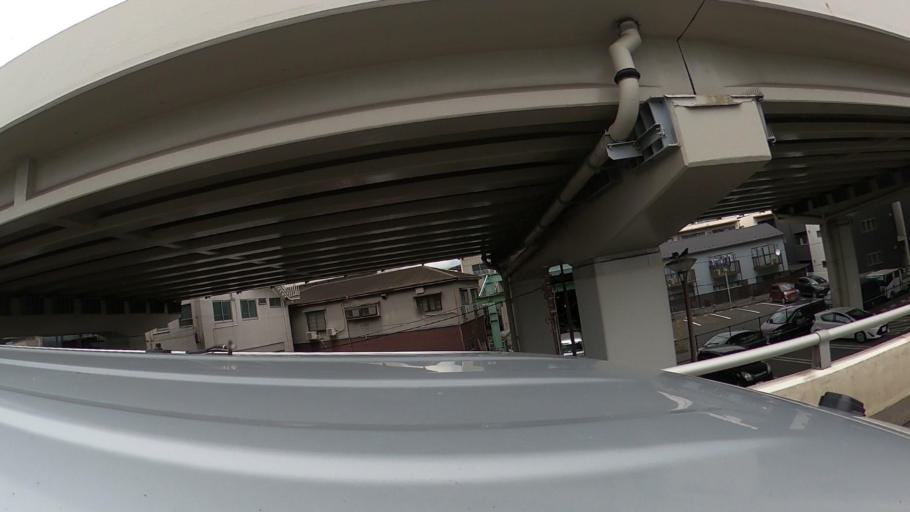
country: JP
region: Kanagawa
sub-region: Kawasaki-shi
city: Kawasaki
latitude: 35.4964
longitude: 139.6840
